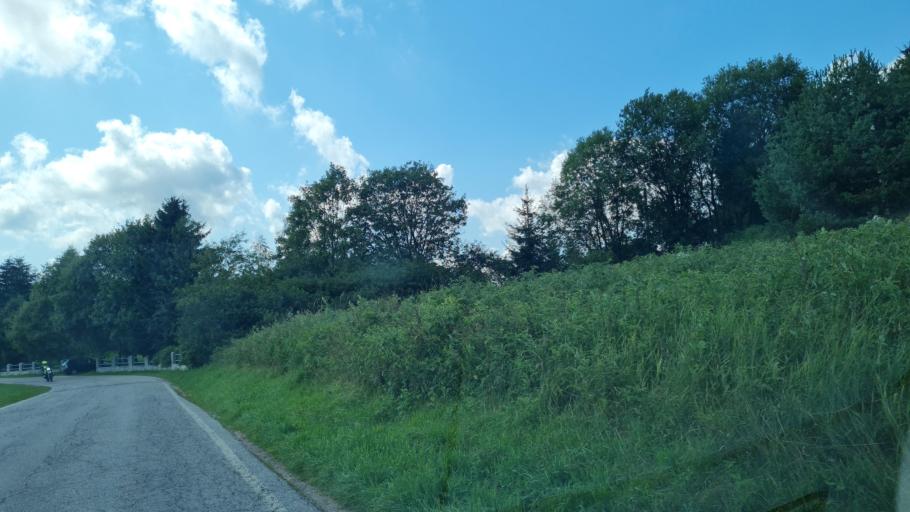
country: IT
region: Veneto
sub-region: Provincia di Vicenza
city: Conco
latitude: 45.8174
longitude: 11.6307
